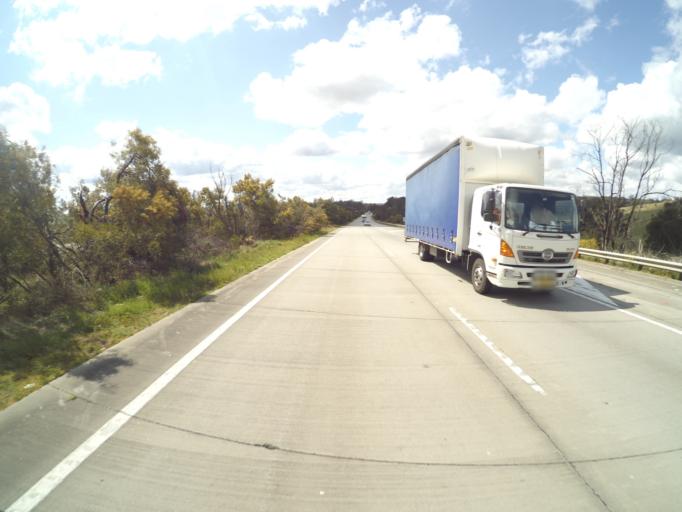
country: AU
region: New South Wales
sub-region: Wingecarribee
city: Bowral
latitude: -34.4523
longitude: 150.3688
